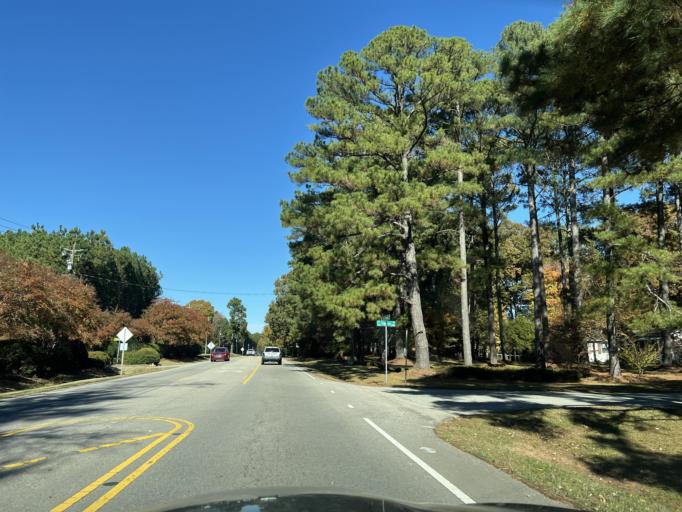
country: US
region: North Carolina
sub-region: Wake County
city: Garner
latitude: 35.7017
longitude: -78.6890
